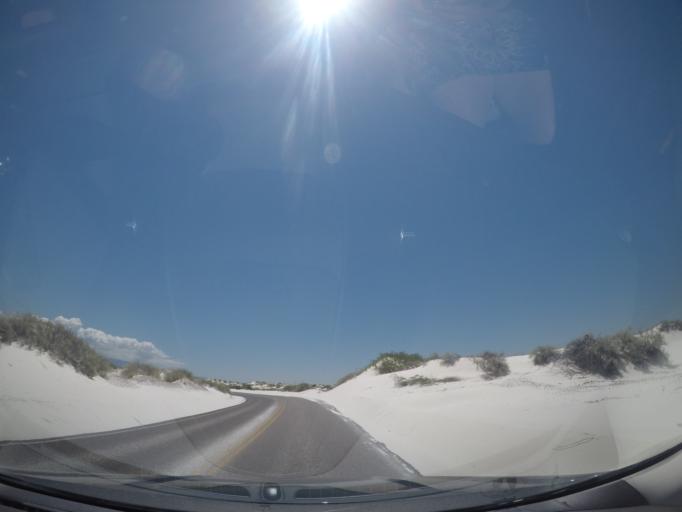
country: US
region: New Mexico
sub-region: Otero County
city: Holloman Air Force Base
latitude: 32.7925
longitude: -106.2364
